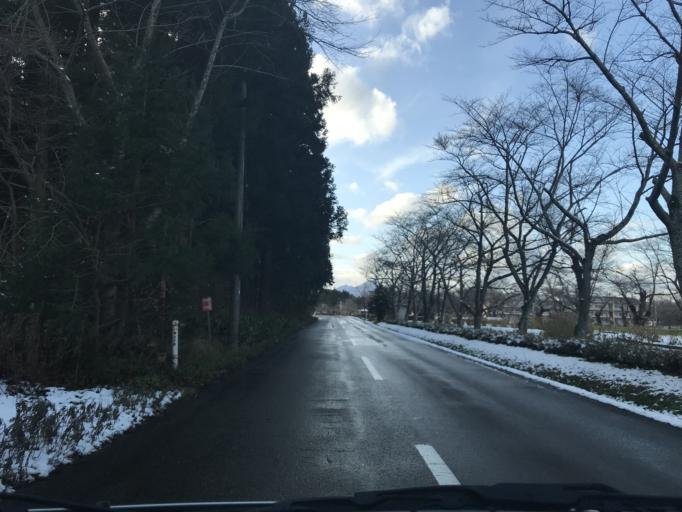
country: JP
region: Iwate
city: Kitakami
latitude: 39.2355
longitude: 141.0484
